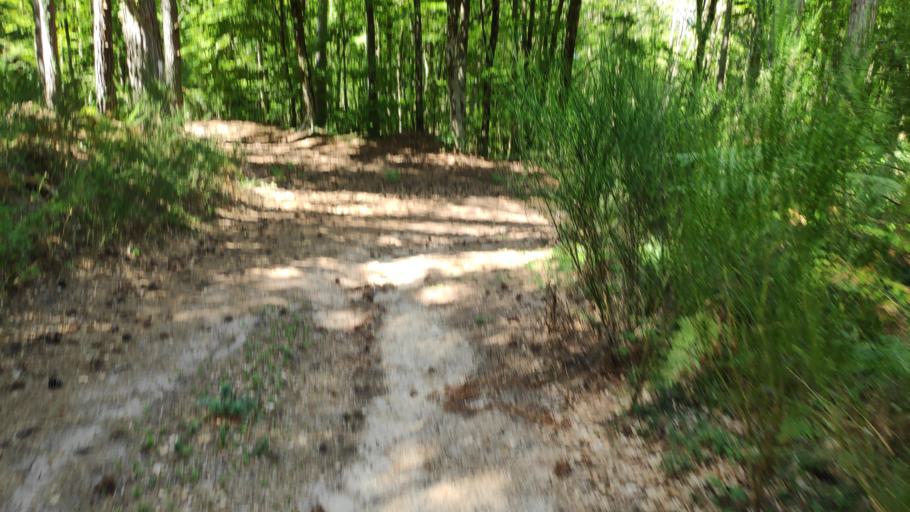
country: IT
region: Calabria
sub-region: Provincia di Vibo-Valentia
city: Nardodipace
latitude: 38.5253
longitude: 16.3869
